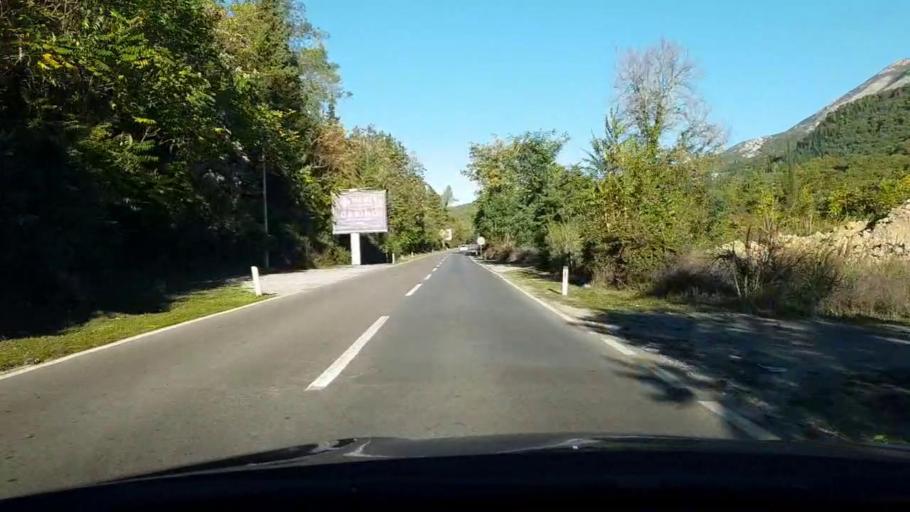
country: ME
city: Igalo
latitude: 42.4769
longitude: 18.4637
